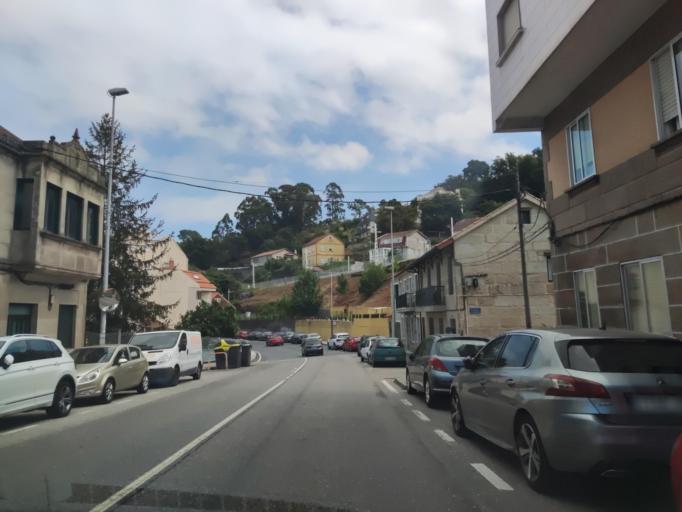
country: ES
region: Galicia
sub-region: Provincia de Pontevedra
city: Vigo
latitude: 42.2626
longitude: -8.6755
